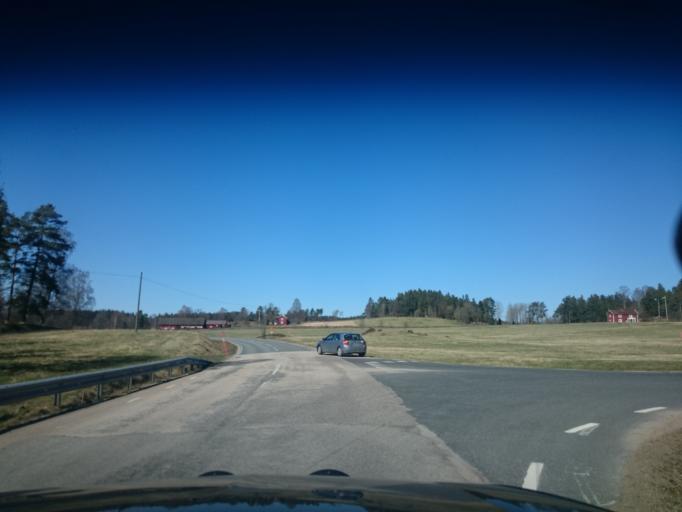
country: SE
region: Joenkoeping
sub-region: Vetlanda Kommun
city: Landsbro
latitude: 57.2189
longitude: 14.9526
